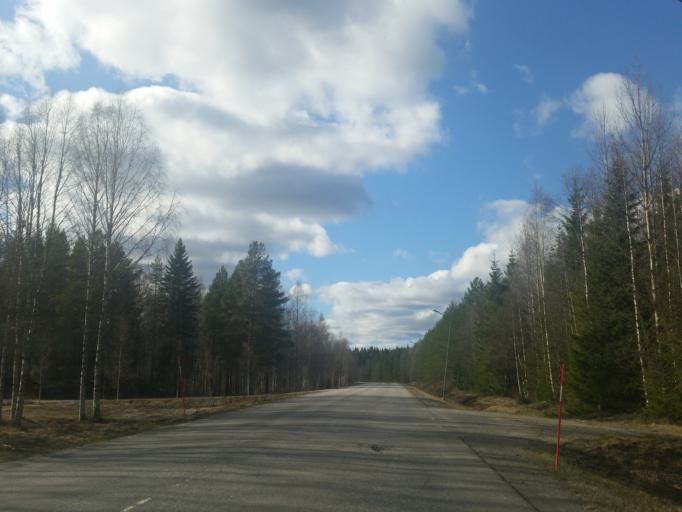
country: SE
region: Vaesterbotten
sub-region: Robertsfors Kommun
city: Robertsfors
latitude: 64.1985
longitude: 20.8353
